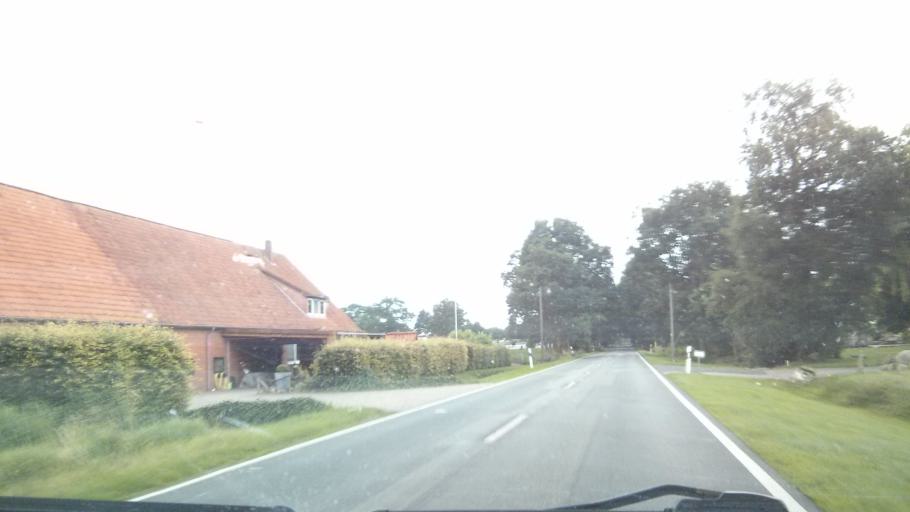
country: DE
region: Lower Saxony
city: Beverstedt
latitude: 53.4729
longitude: 8.8511
